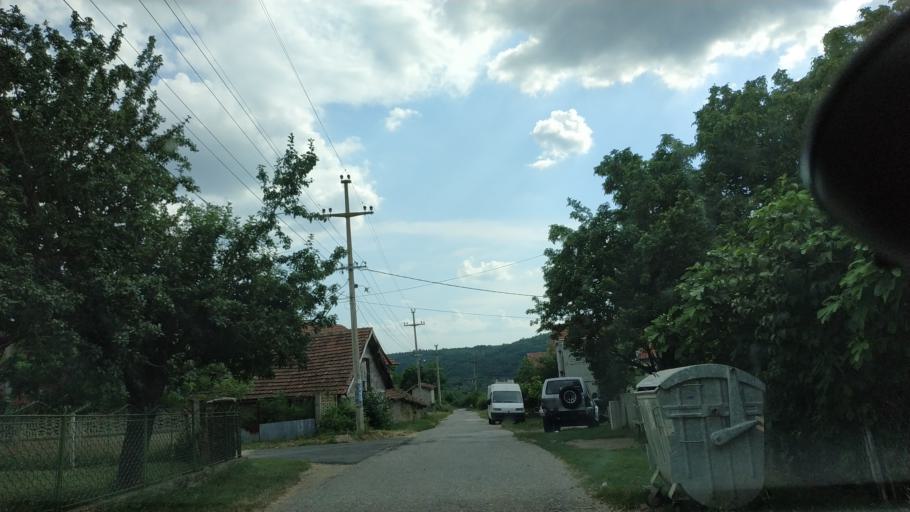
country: RS
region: Central Serbia
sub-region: Nisavski Okrug
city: Aleksinac
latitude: 43.6027
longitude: 21.6883
